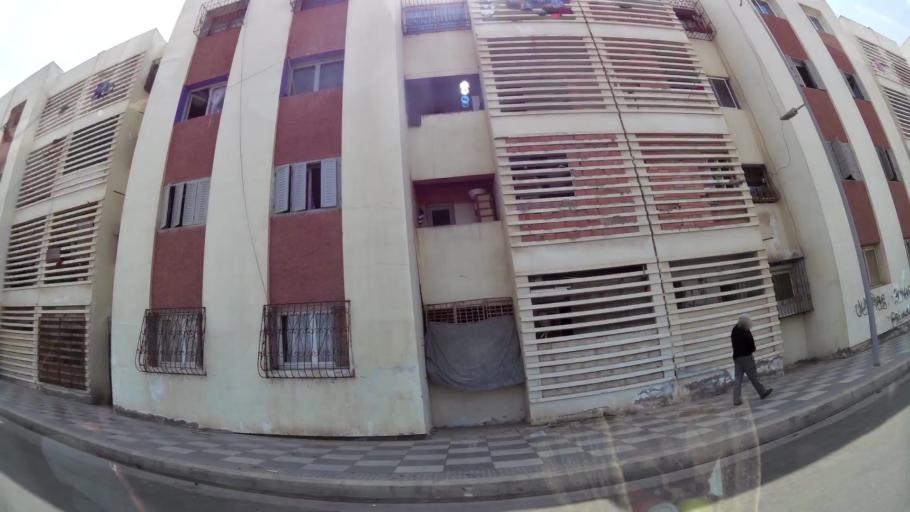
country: MA
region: Rabat-Sale-Zemmour-Zaer
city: Sale
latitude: 34.0583
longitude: -6.8166
